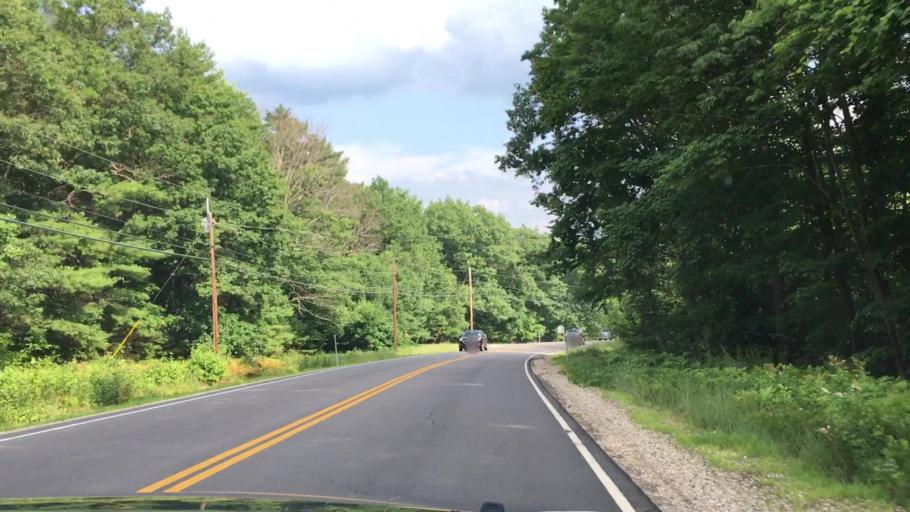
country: US
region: New Hampshire
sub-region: Belknap County
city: Gilford
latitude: 43.5658
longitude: -71.3377
